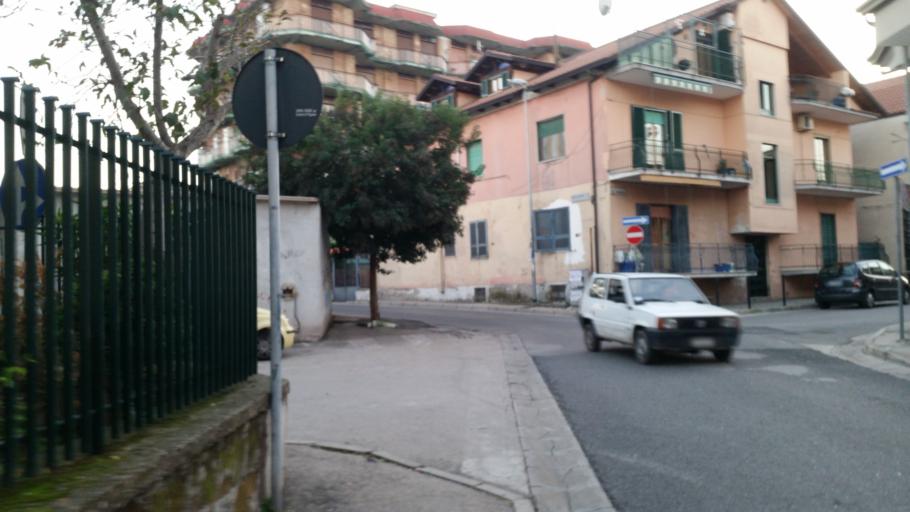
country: IT
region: Campania
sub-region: Provincia di Napoli
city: Mugnano di Napoli
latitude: 40.9074
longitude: 14.2110
